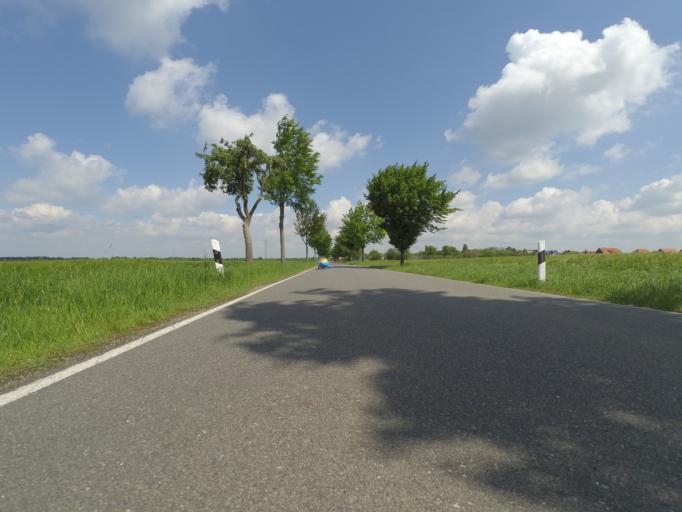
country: DE
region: Lower Saxony
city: Peine
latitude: 52.2995
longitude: 10.3034
